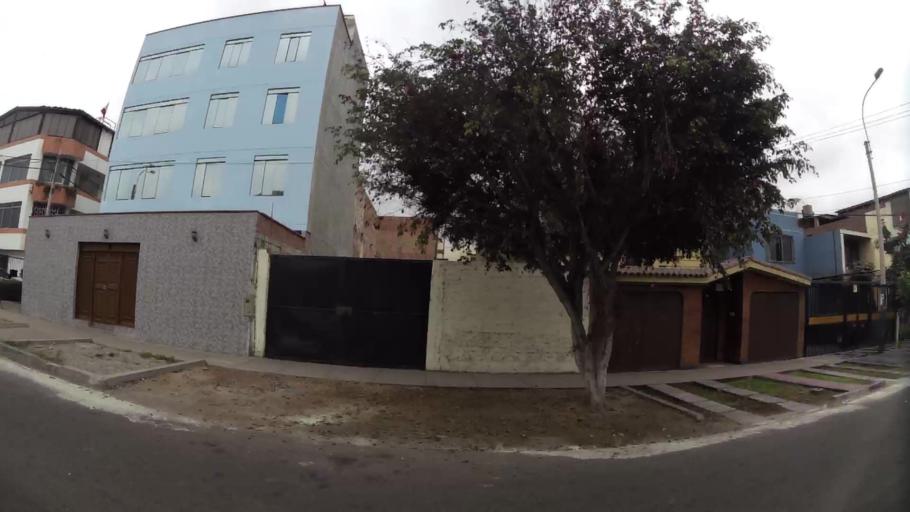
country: PE
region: Lima
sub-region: Lima
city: Surco
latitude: -12.1453
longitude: -76.9924
